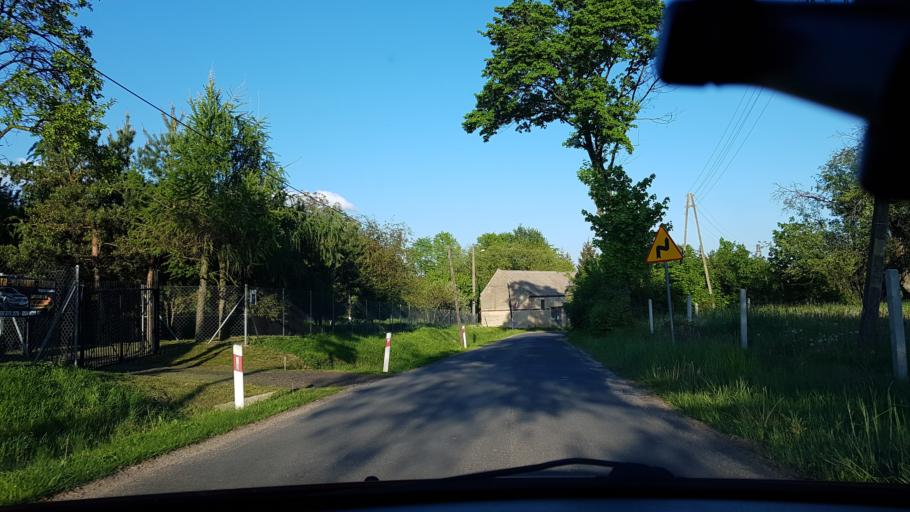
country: PL
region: Lower Silesian Voivodeship
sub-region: Powiat zabkowicki
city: Budzow
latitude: 50.6106
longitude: 16.7058
